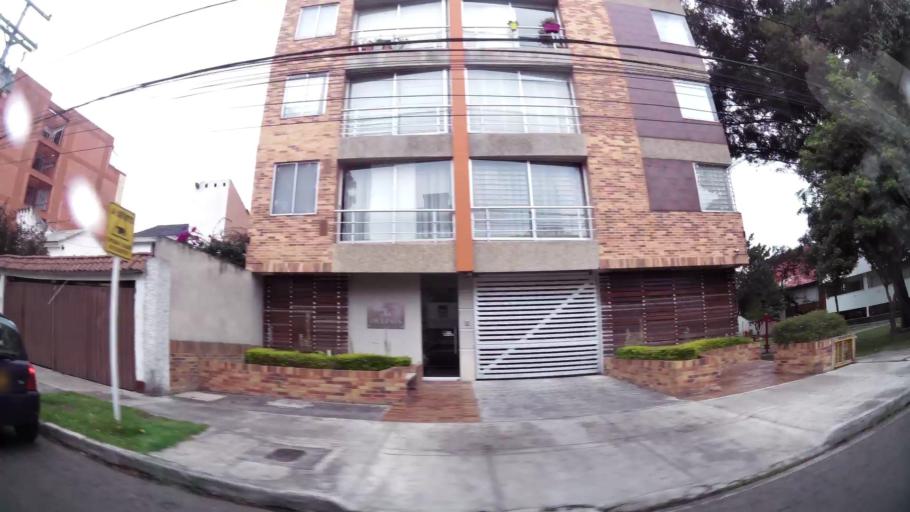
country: CO
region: Bogota D.C.
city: Barrio San Luis
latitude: 4.7219
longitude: -74.0450
